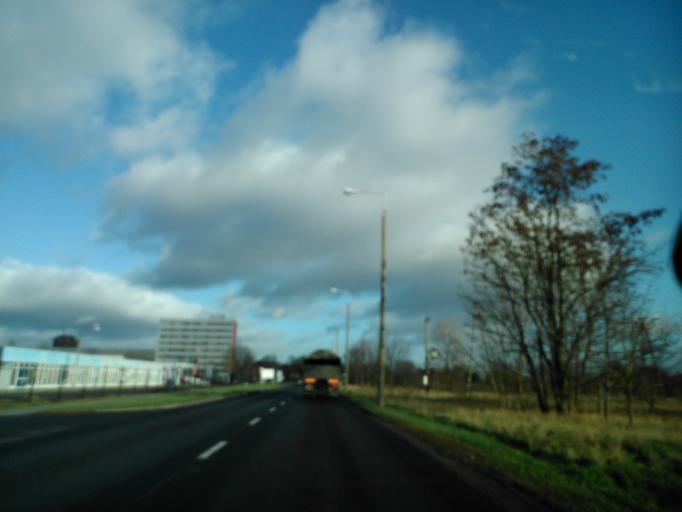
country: PL
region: Kujawsko-Pomorskie
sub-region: Torun
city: Torun
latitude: 52.9838
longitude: 18.5766
